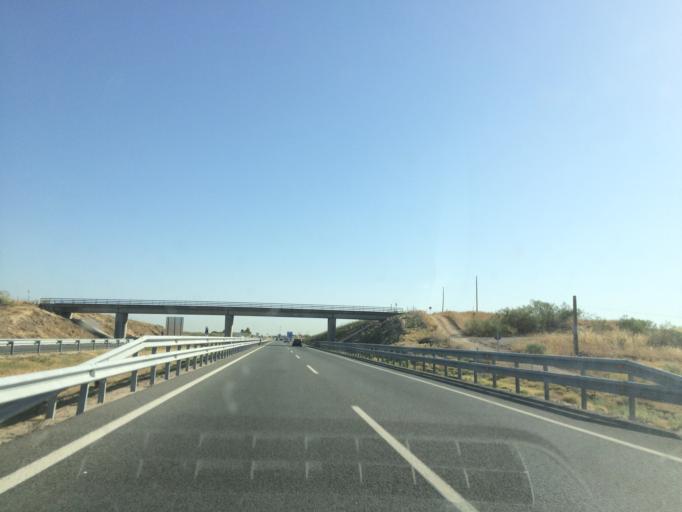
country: ES
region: Castille-La Mancha
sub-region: Province of Toledo
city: Valmojado
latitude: 40.2273
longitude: -4.0717
